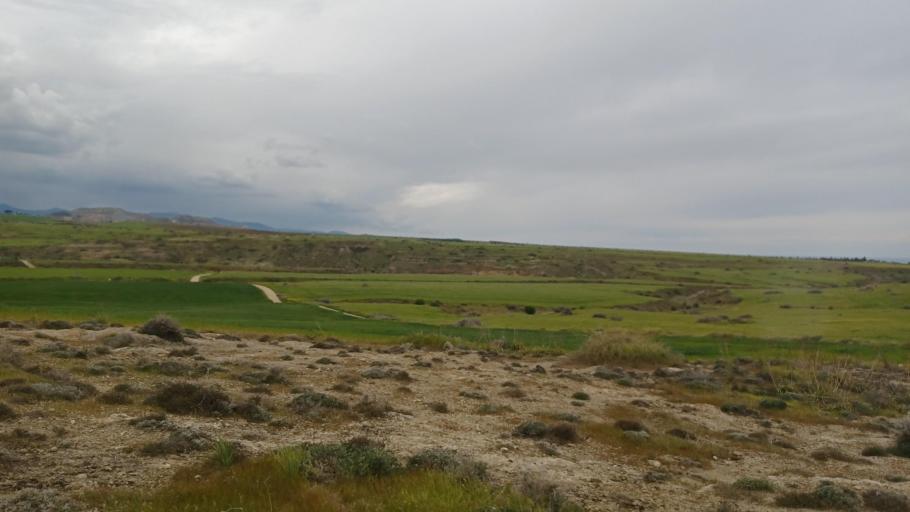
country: CY
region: Lefkosia
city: Astromeritis
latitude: 35.1014
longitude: 32.9487
